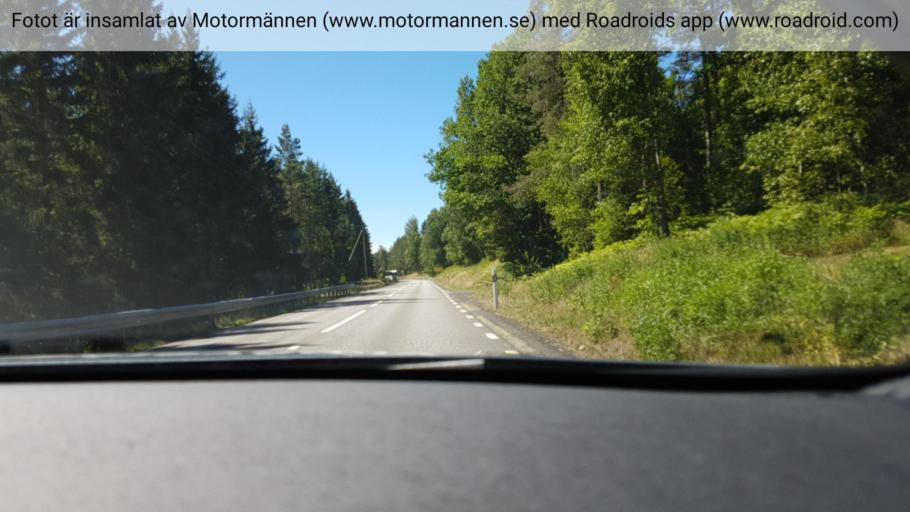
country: SE
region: Joenkoeping
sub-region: Mullsjo Kommun
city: Mullsjoe
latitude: 57.7928
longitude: 13.8393
